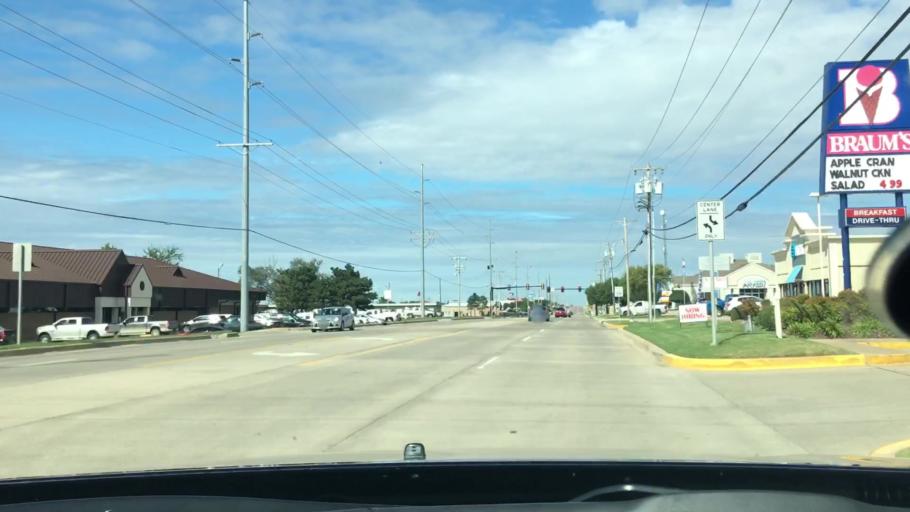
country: US
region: Oklahoma
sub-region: Pontotoc County
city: Ada
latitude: 34.7835
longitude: -96.6523
